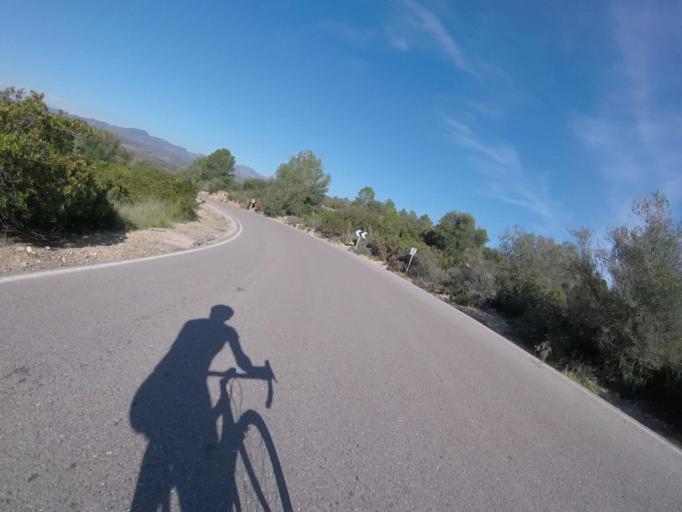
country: ES
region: Valencia
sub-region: Provincia de Castello
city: Benlloch
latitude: 40.2457
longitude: 0.0789
